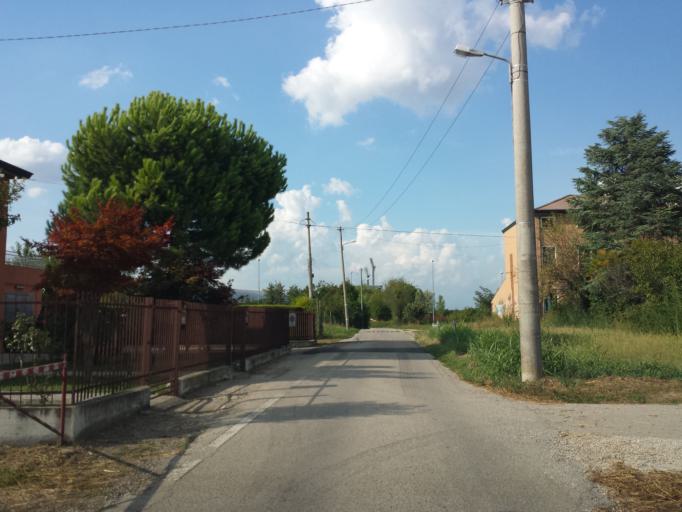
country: IT
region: Veneto
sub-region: Provincia di Padova
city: Padova
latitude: 45.4270
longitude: 11.8586
